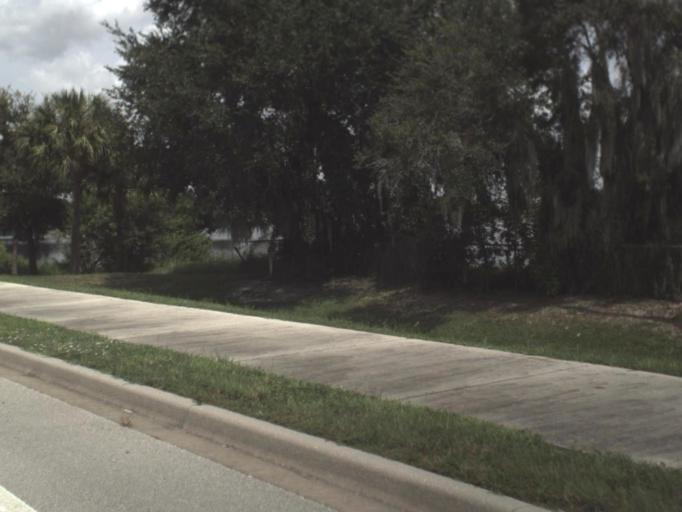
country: US
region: Florida
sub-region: Highlands County
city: Avon Park
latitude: 27.5784
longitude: -81.5143
